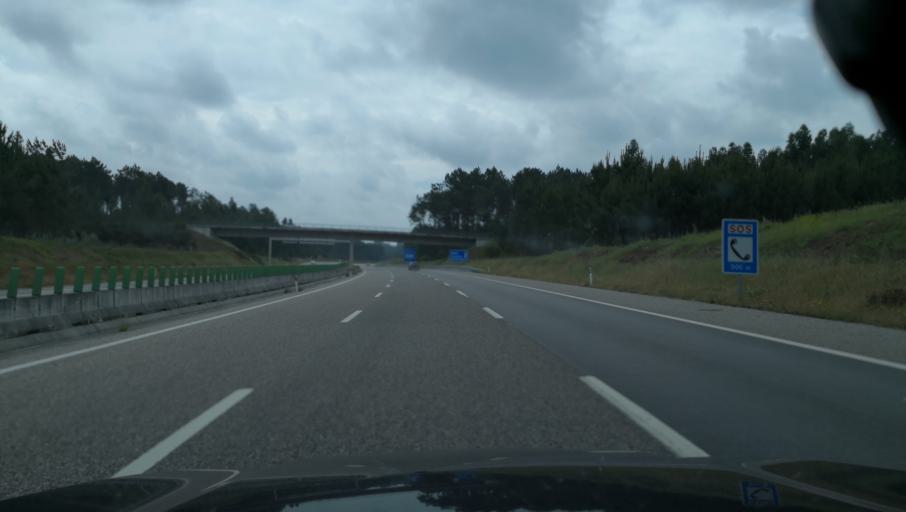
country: PT
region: Leiria
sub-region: Pombal
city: Lourical
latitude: 39.9868
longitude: -8.7929
